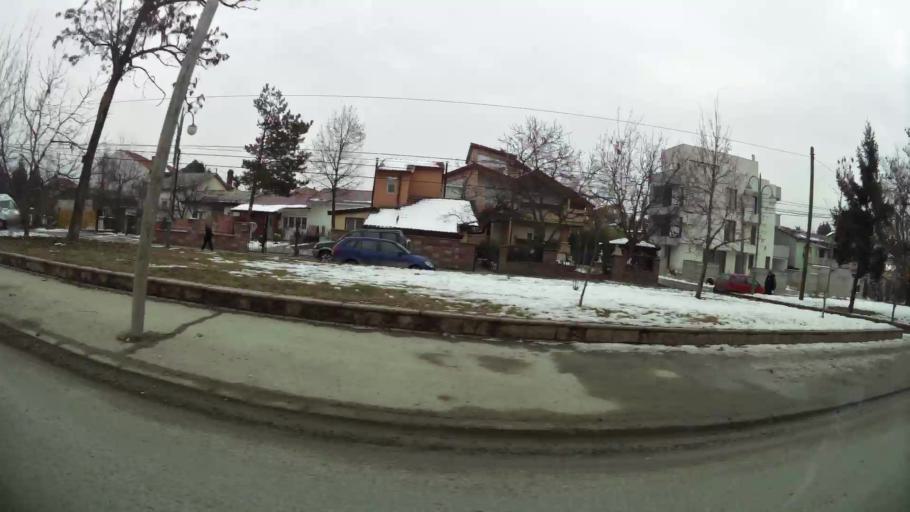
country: MK
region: Butel
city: Butel
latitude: 42.0335
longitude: 21.4456
